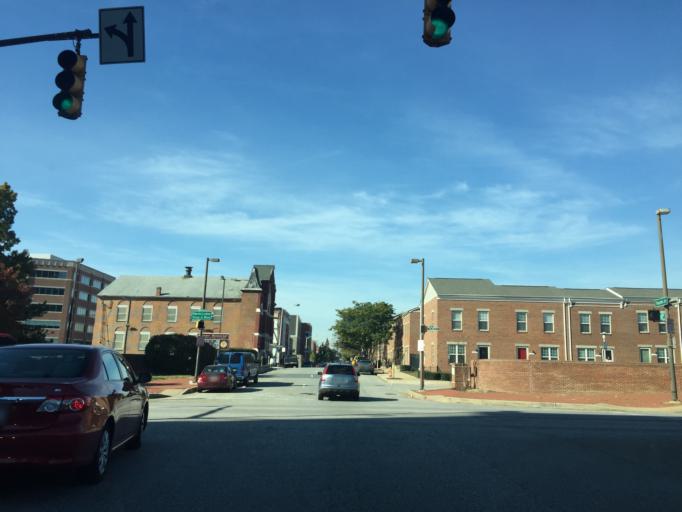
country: US
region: Maryland
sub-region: City of Baltimore
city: Baltimore
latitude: 39.2901
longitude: -76.6275
